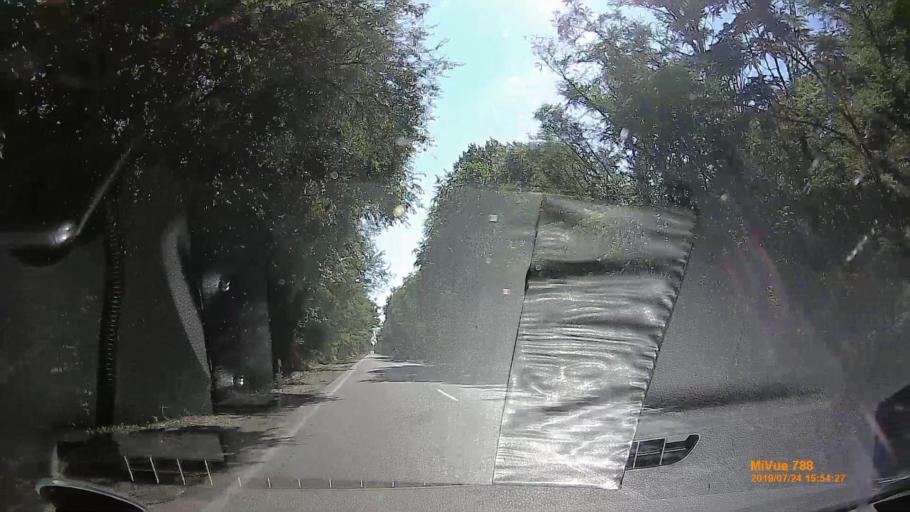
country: HU
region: Szabolcs-Szatmar-Bereg
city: Vaja
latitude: 48.0121
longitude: 22.1322
